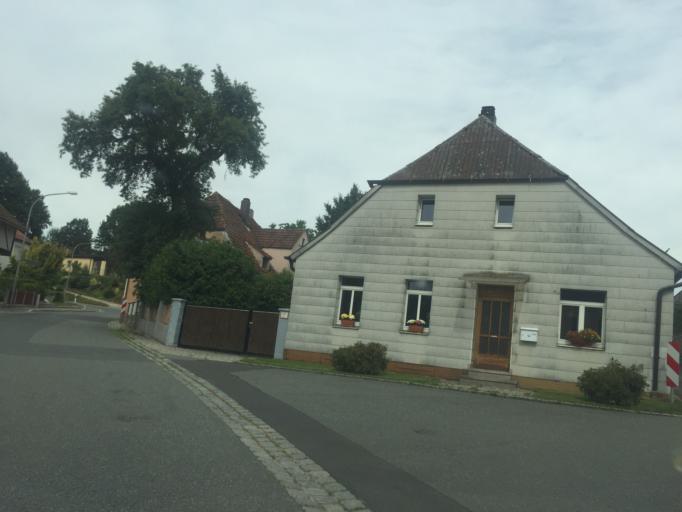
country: DE
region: Bavaria
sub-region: Upper Palatinate
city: Pressath
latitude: 49.7711
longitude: 11.9330
